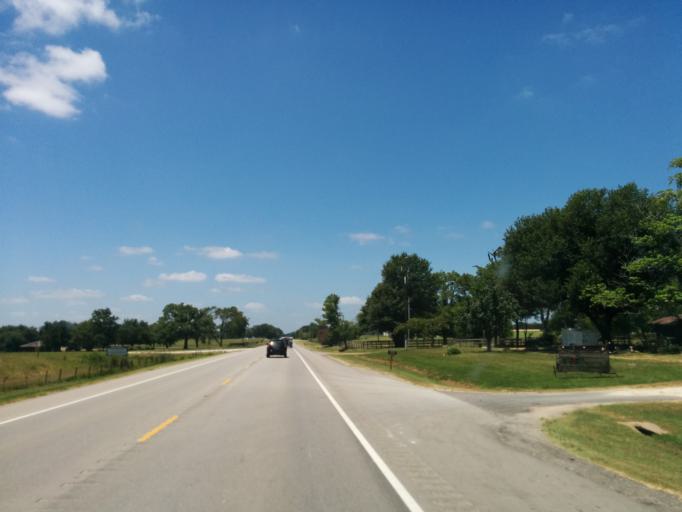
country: US
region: Texas
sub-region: Leon County
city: Hilltop Lakes
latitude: 30.8941
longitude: -96.1563
